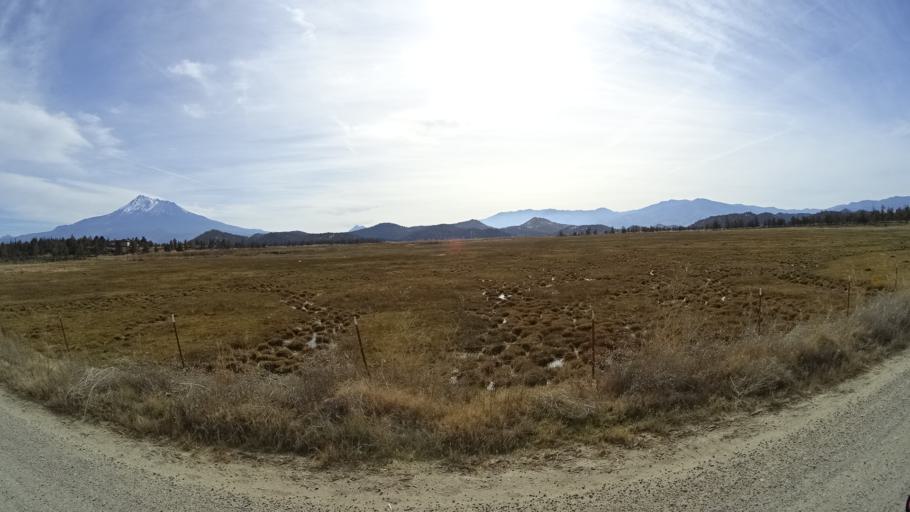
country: US
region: California
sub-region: Siskiyou County
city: Montague
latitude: 41.5954
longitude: -122.4212
